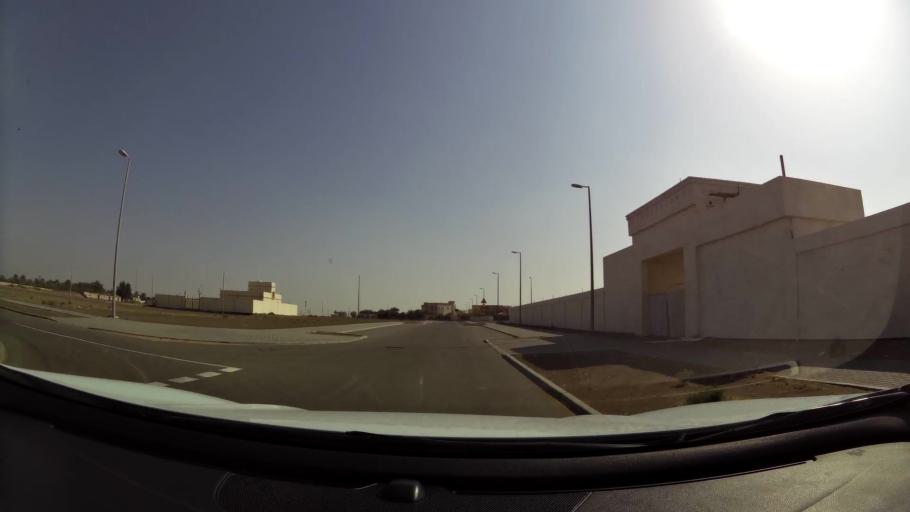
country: AE
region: Abu Dhabi
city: Al Ain
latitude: 24.0899
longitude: 55.9025
